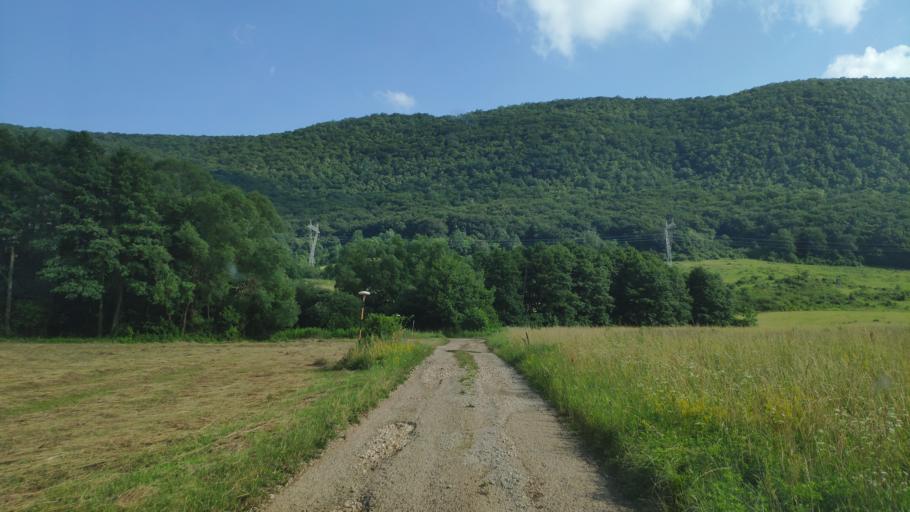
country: HU
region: Borsod-Abauj-Zemplen
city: Szendro
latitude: 48.5867
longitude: 20.7305
